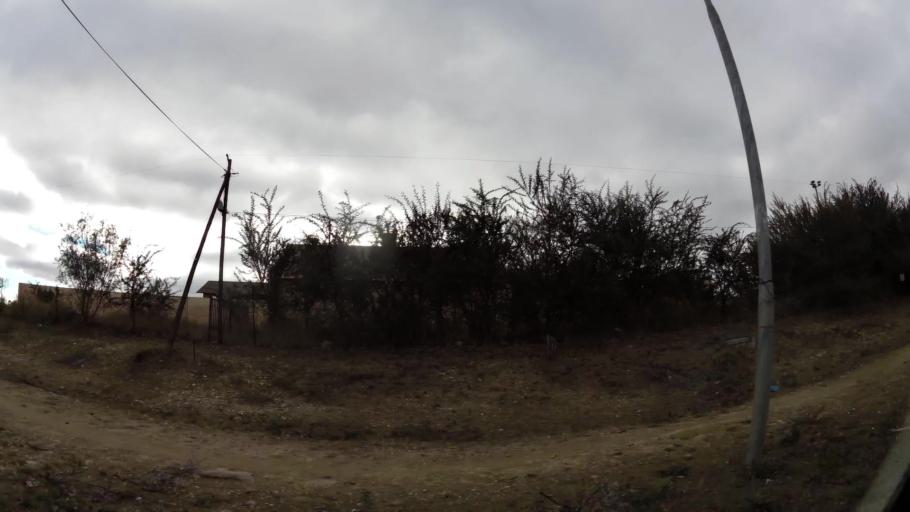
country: ZA
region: Limpopo
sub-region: Capricorn District Municipality
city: Polokwane
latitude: -23.9269
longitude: 29.4495
